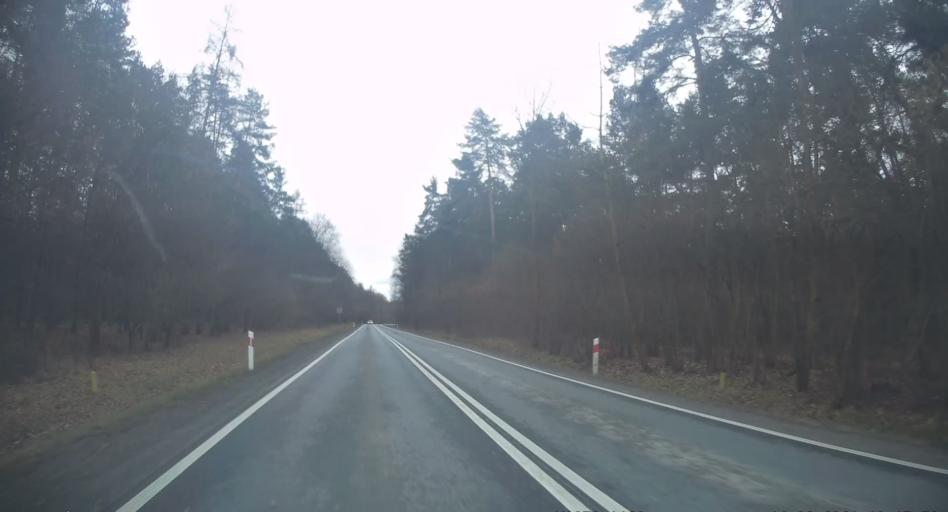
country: PL
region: Lesser Poland Voivodeship
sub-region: Powiat wielicki
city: Niepolomice
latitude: 50.0196
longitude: 20.2378
